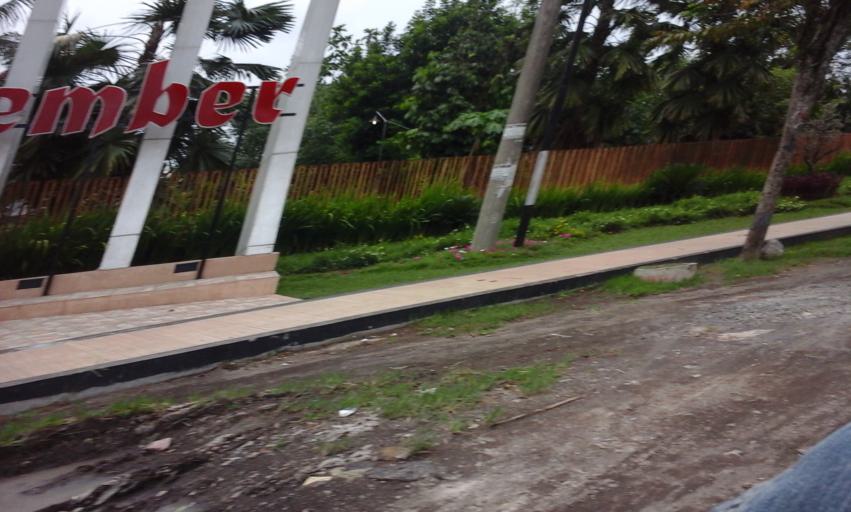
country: ID
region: East Java
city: Mangli
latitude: -8.1922
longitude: 113.6465
